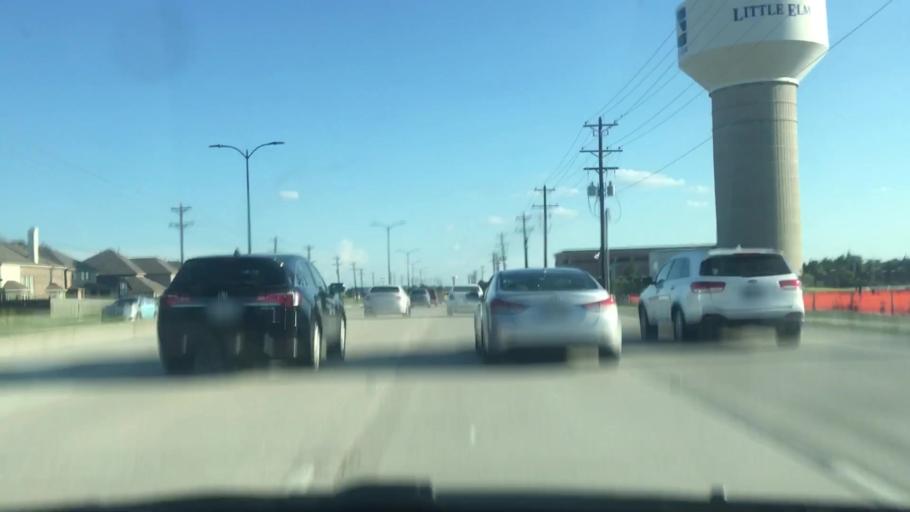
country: US
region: Texas
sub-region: Denton County
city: Little Elm
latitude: 33.1877
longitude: -96.8871
